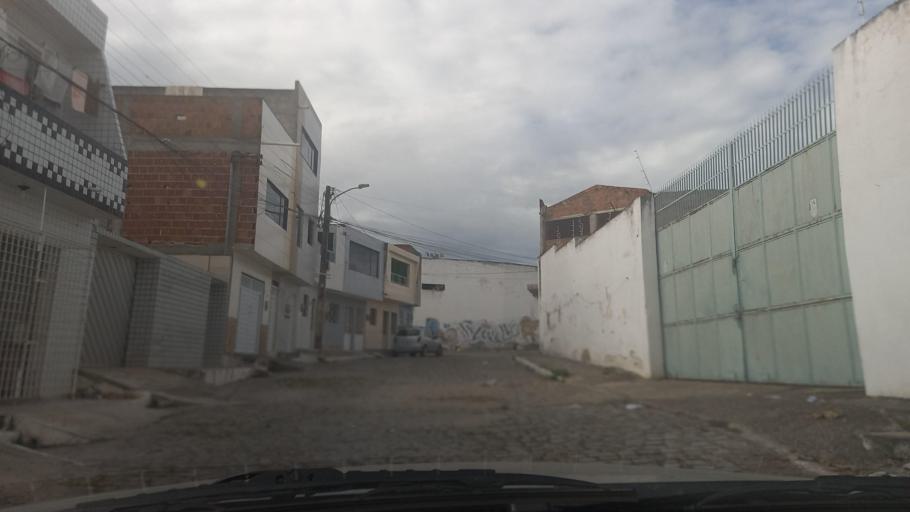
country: BR
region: Pernambuco
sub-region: Caruaru
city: Caruaru
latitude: -8.2919
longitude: -35.9812
